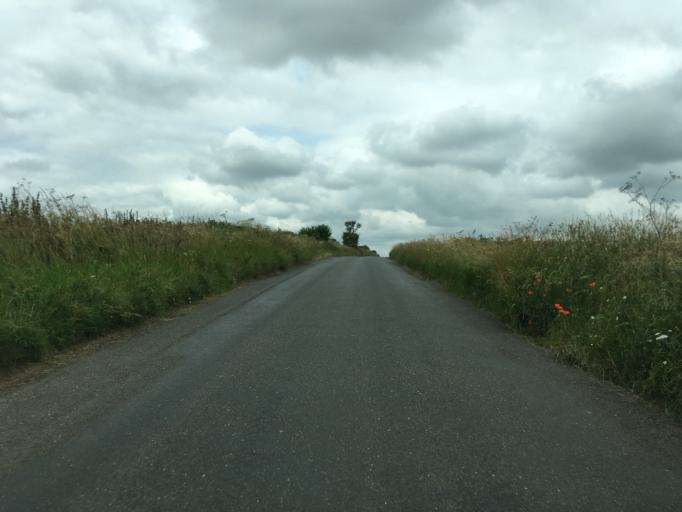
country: GB
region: England
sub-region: Oxfordshire
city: Charlbury
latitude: 51.9154
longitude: -1.4703
